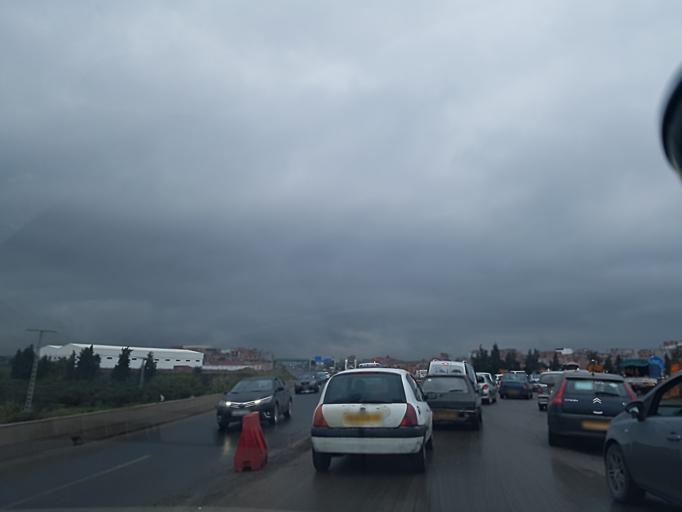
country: DZ
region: Boumerdes
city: Ouled Moussa
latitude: 36.6741
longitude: 3.3760
